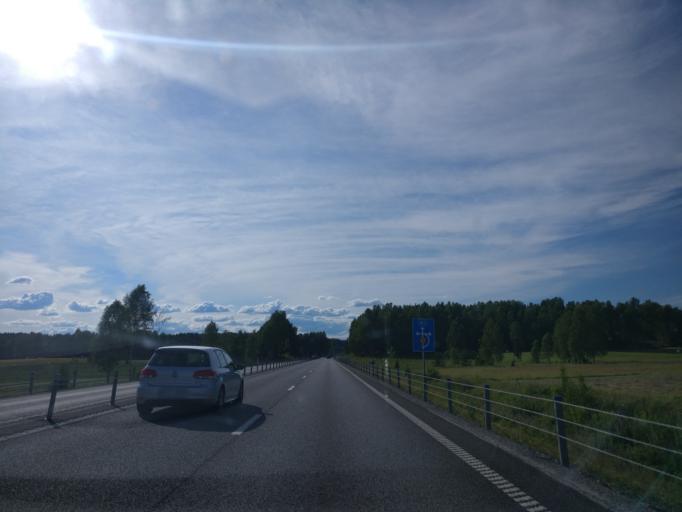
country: SE
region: Vaermland
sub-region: Arvika Kommun
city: Arvika
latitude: 59.6532
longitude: 12.6620
